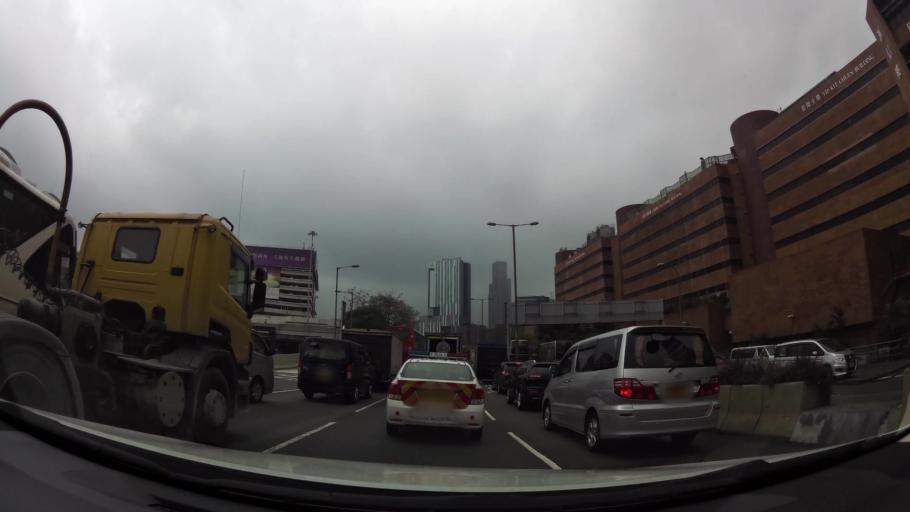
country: HK
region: Kowloon City
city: Kowloon
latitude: 22.3052
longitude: 114.1815
